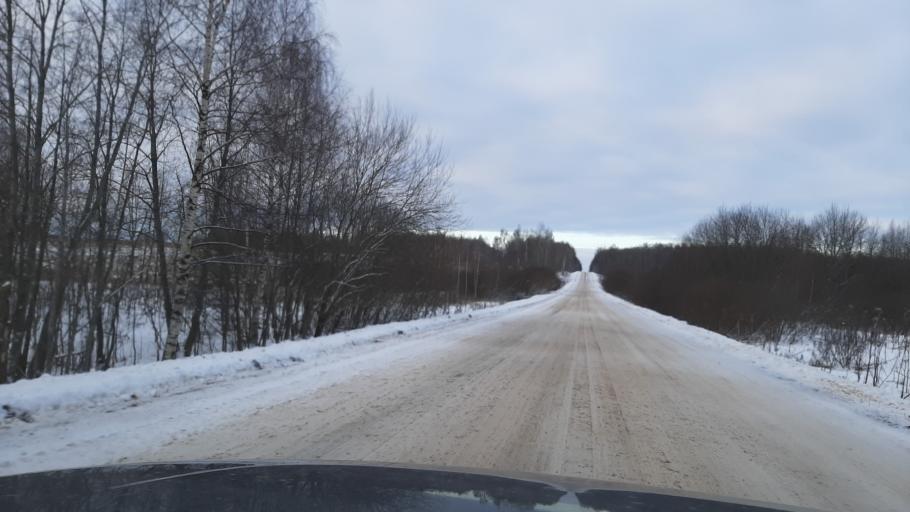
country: RU
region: Kostroma
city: Kosmynino
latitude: 57.4811
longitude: 40.7619
